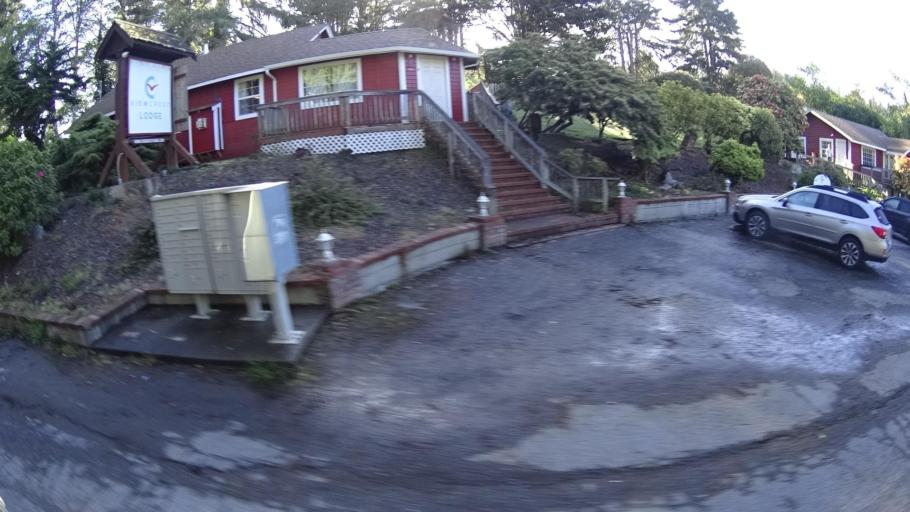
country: US
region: California
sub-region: Humboldt County
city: Westhaven-Moonstone
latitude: 41.1219
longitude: -124.1566
